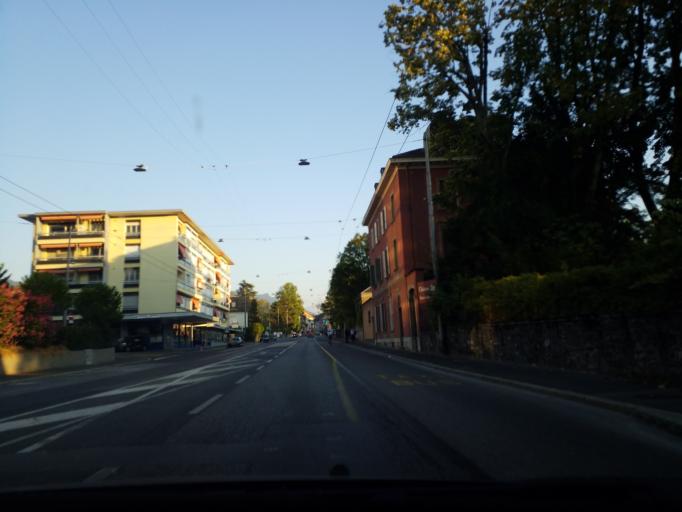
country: CH
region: Vaud
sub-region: Riviera-Pays-d'Enhaut District
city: La Tour-de-Peilz
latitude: 46.4562
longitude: 6.8540
